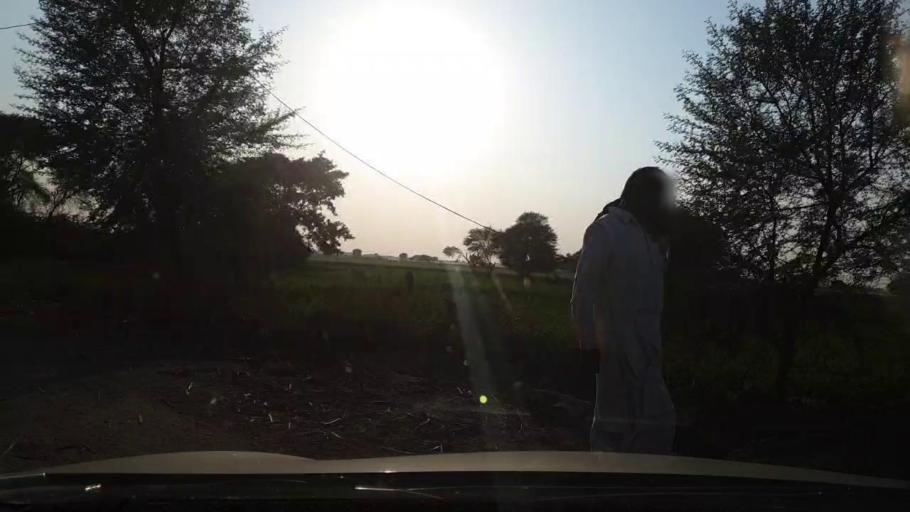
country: PK
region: Sindh
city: Tando Adam
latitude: 25.6958
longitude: 68.7314
